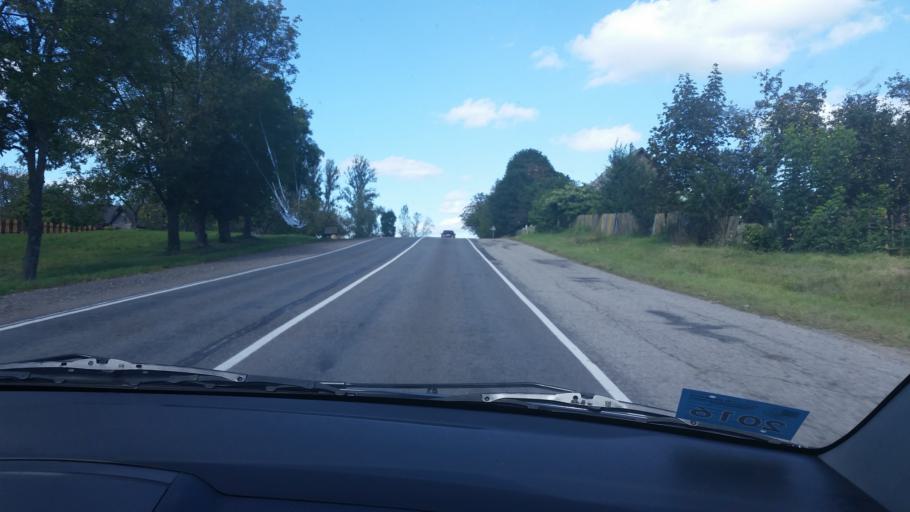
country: BY
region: Vitebsk
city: Vitebsk
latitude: 55.1102
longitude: 30.2831
